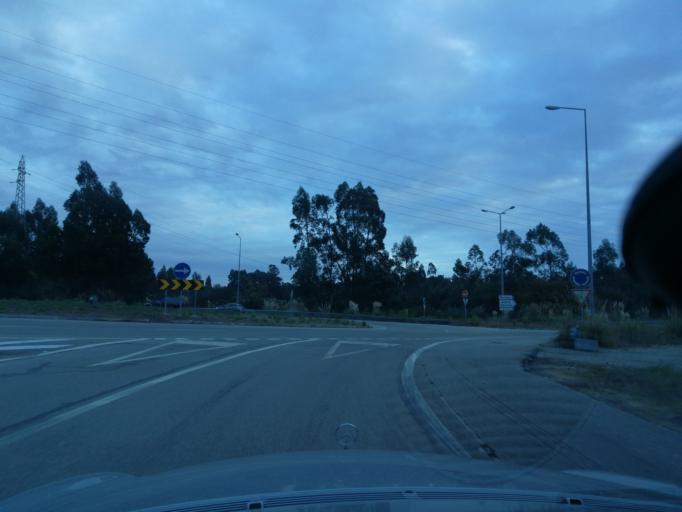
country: PT
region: Aveiro
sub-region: Estarreja
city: Beduido
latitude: 40.7841
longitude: -8.5599
